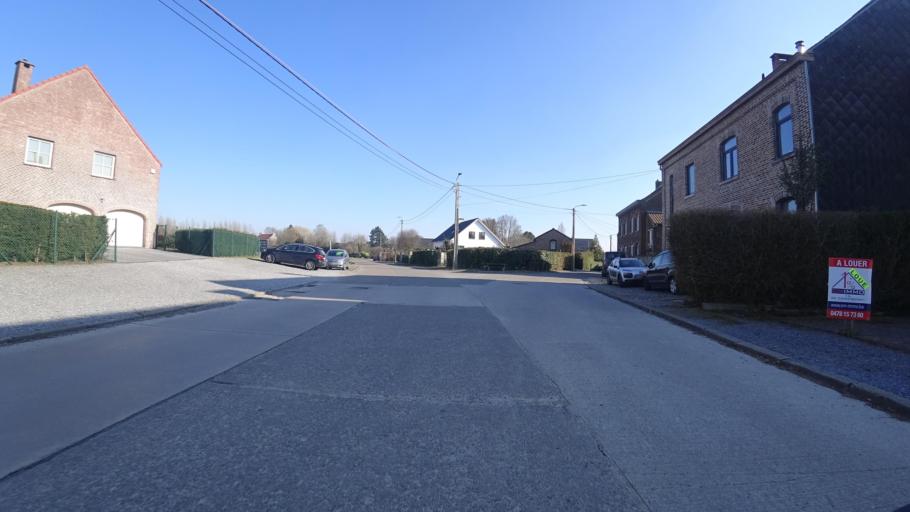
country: BE
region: Wallonia
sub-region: Province de Namur
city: Gembloux
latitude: 50.5639
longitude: 4.6799
